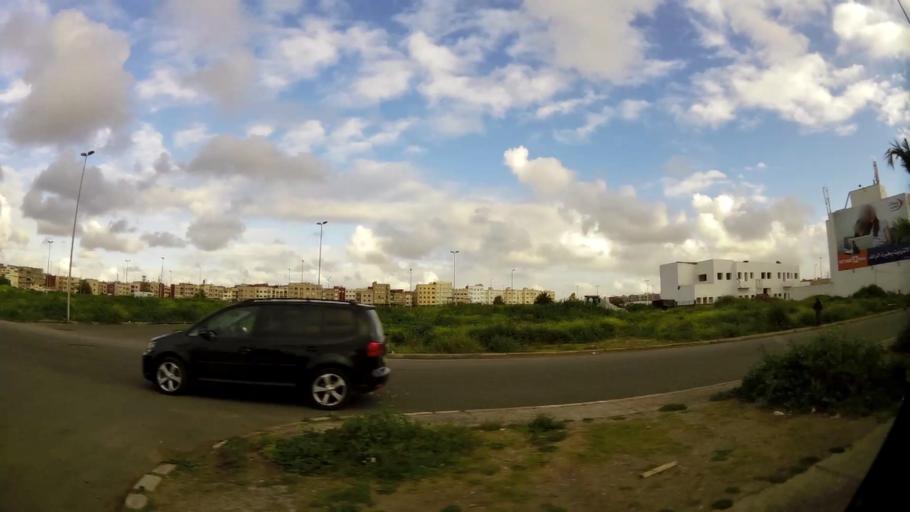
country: MA
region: Grand Casablanca
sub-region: Mohammedia
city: Mohammedia
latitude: 33.6845
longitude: -7.3844
